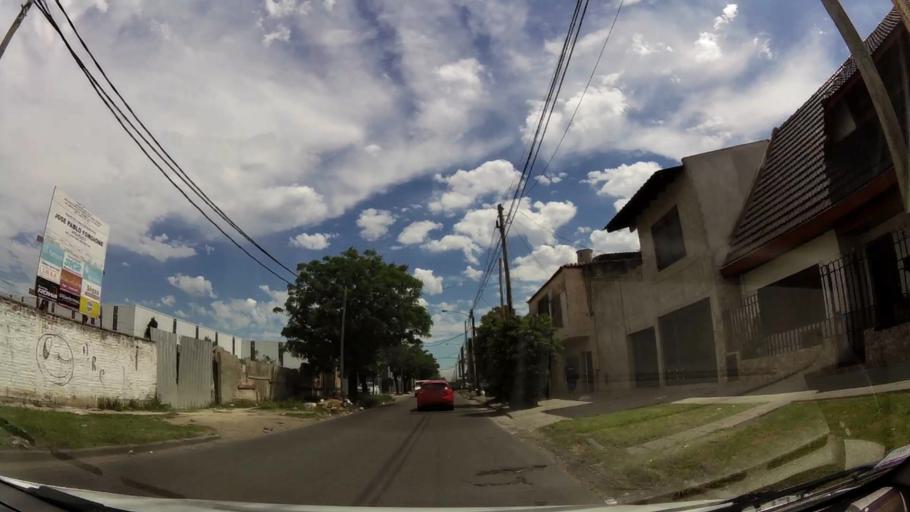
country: AR
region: Buenos Aires
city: San Justo
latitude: -34.6869
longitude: -58.5466
